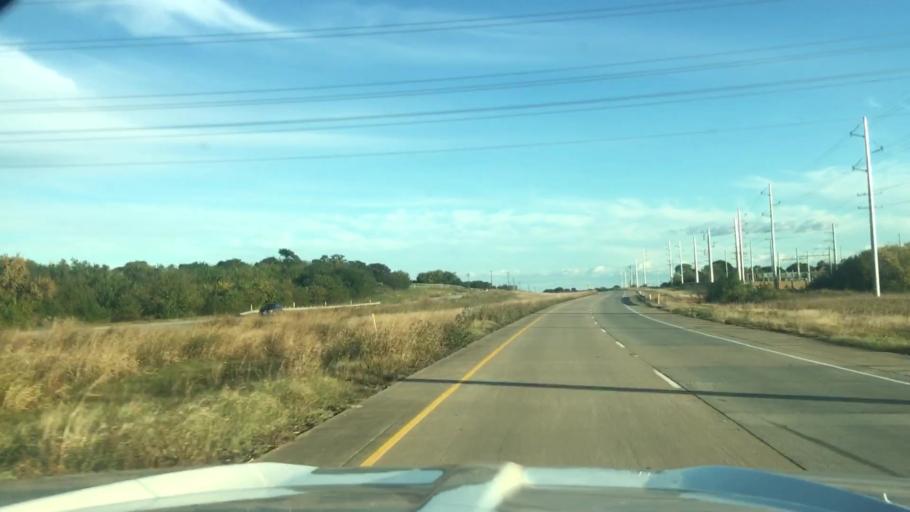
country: US
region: Texas
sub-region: Denton County
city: Denton
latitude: 33.2530
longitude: -97.1011
